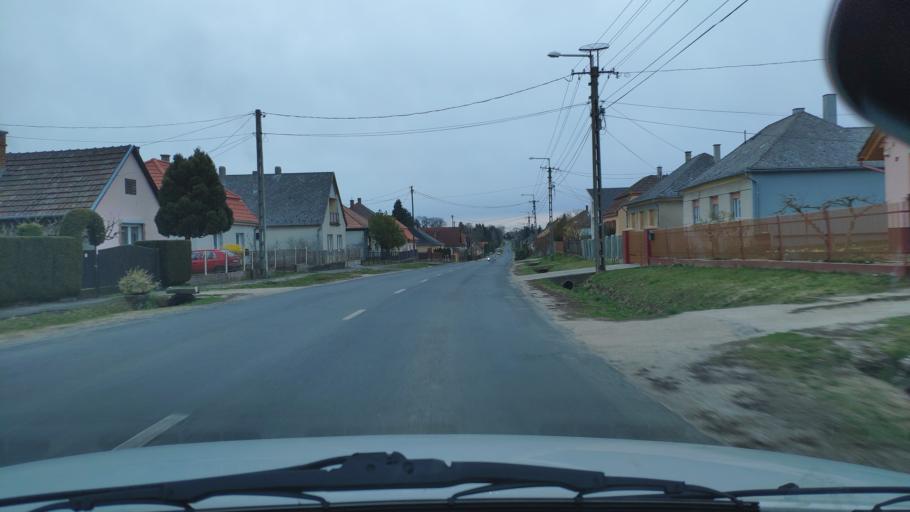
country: HU
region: Zala
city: Nagykanizsa
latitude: 46.5029
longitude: 16.9867
